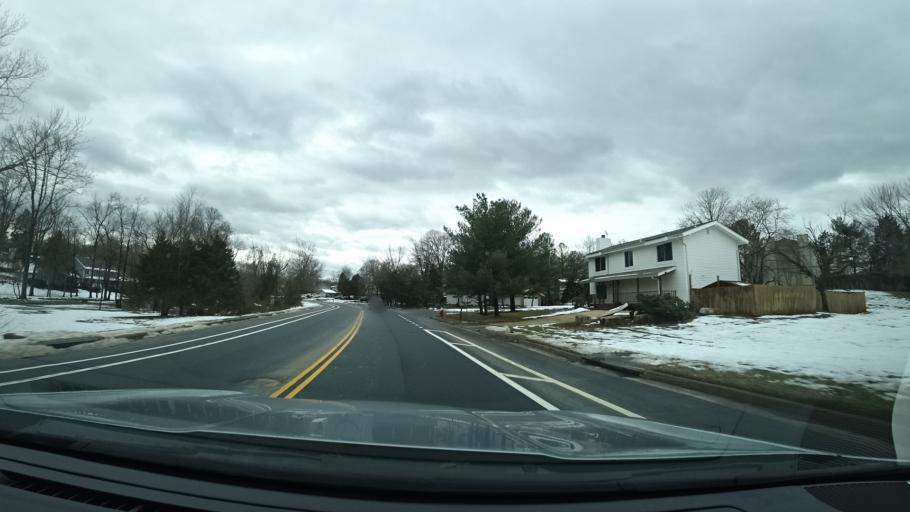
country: US
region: Virginia
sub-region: Loudoun County
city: Oak Grove
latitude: 39.0079
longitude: -77.3896
